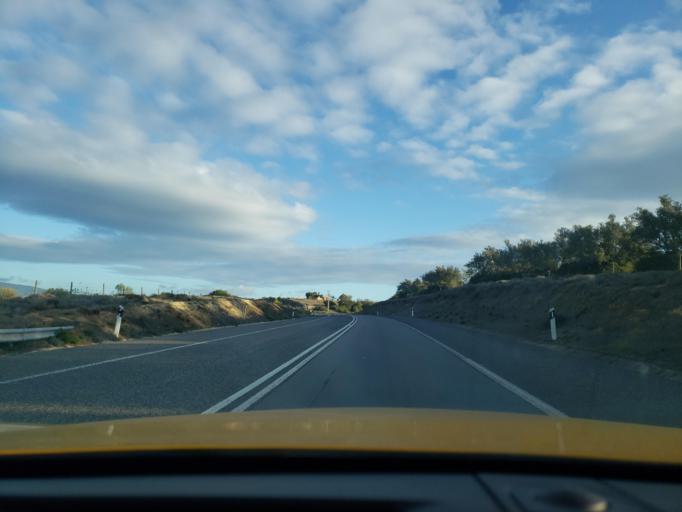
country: PT
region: Faro
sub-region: Portimao
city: Portimao
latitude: 37.1687
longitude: -8.5686
